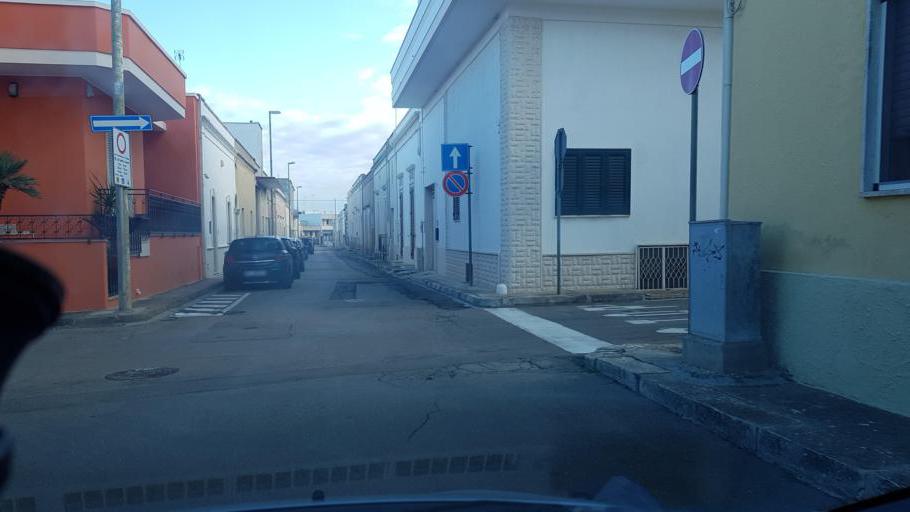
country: IT
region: Apulia
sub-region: Provincia di Lecce
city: Veglie
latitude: 40.3371
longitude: 17.9718
